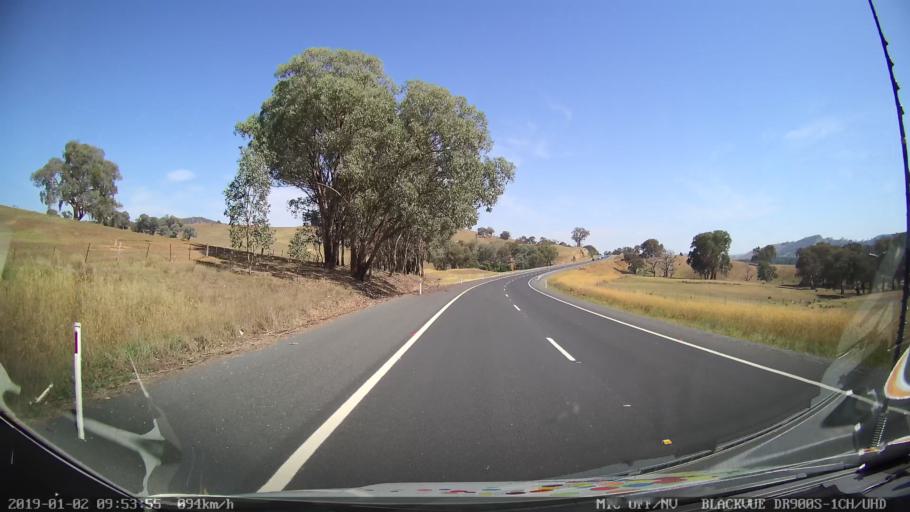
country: AU
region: New South Wales
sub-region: Tumut Shire
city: Tumut
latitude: -35.2421
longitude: 148.1990
